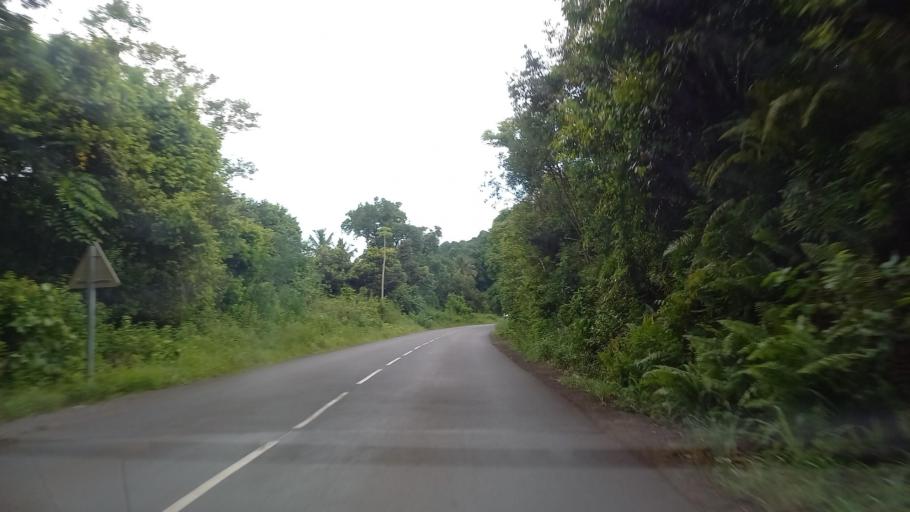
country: YT
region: M'Tsangamouji
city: M'Tsangamouji
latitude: -12.7539
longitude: 45.1122
